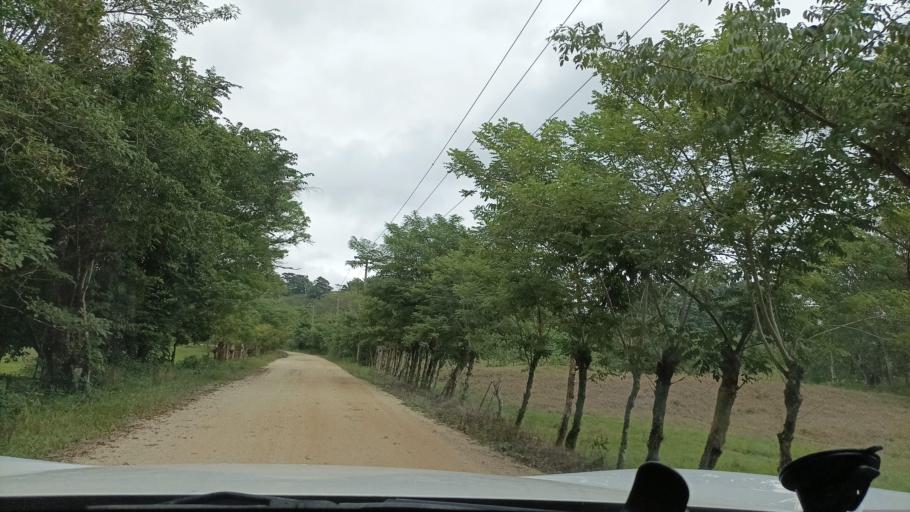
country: MX
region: Veracruz
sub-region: Moloacan
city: Cuichapa
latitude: 17.8320
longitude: -94.3529
